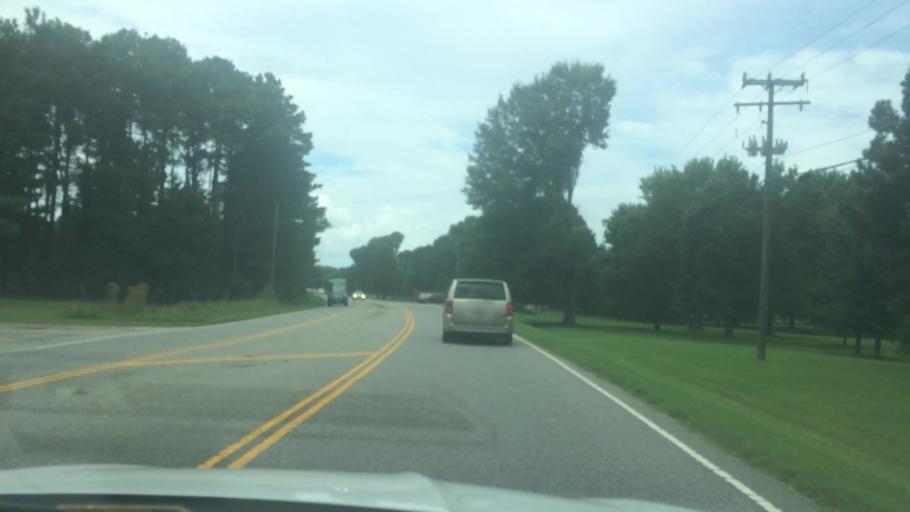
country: US
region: Virginia
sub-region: James City County
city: Williamsburg
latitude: 37.2638
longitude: -76.7614
